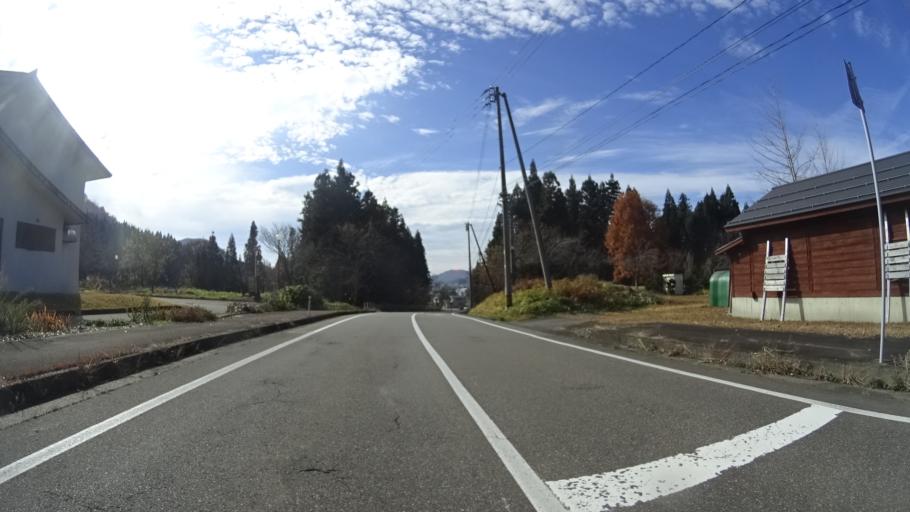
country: JP
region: Niigata
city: Tochio-honcho
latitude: 37.2855
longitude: 138.9959
